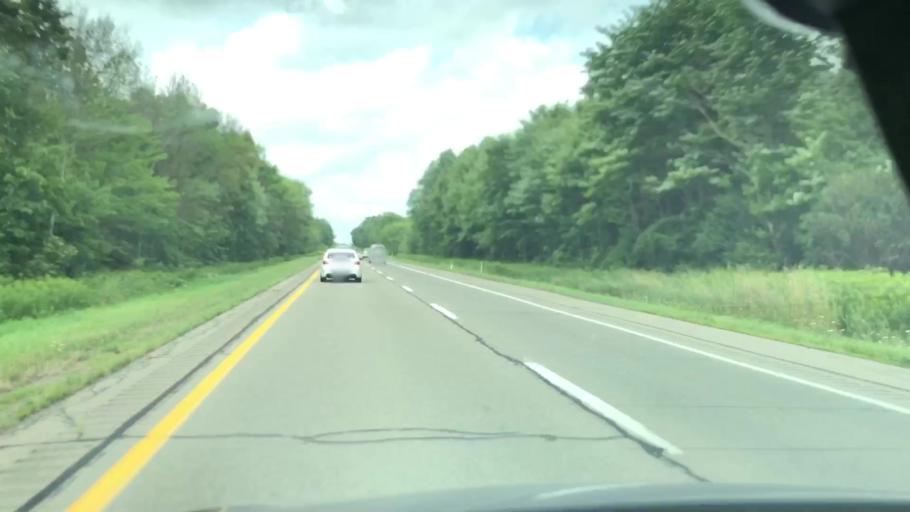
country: US
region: Pennsylvania
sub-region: Crawford County
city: Meadville
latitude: 41.7473
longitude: -80.1973
